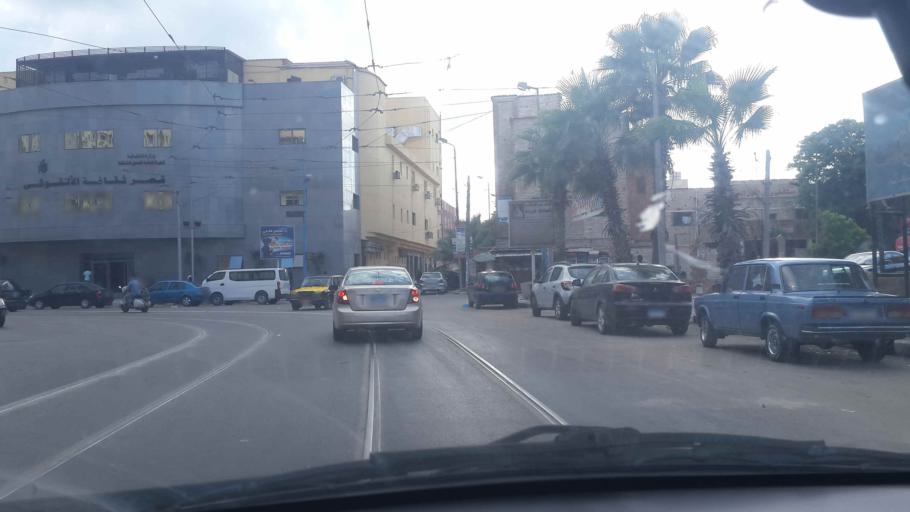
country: EG
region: Alexandria
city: Alexandria
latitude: 31.2099
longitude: 29.8795
